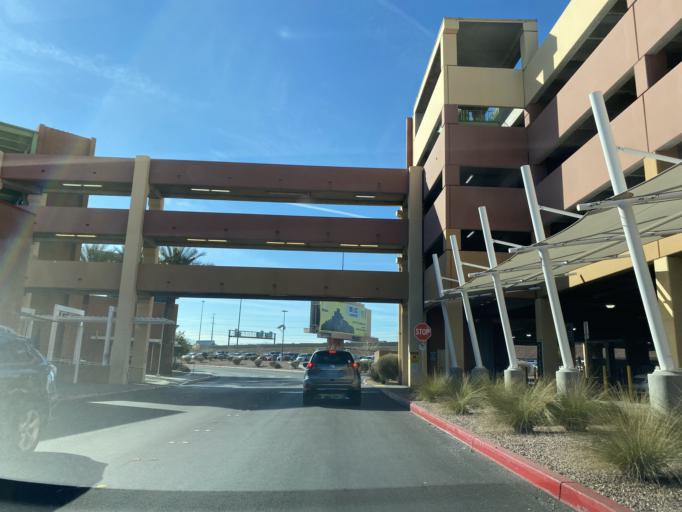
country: US
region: Nevada
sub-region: Clark County
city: Las Vegas
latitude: 36.1656
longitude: -115.1582
